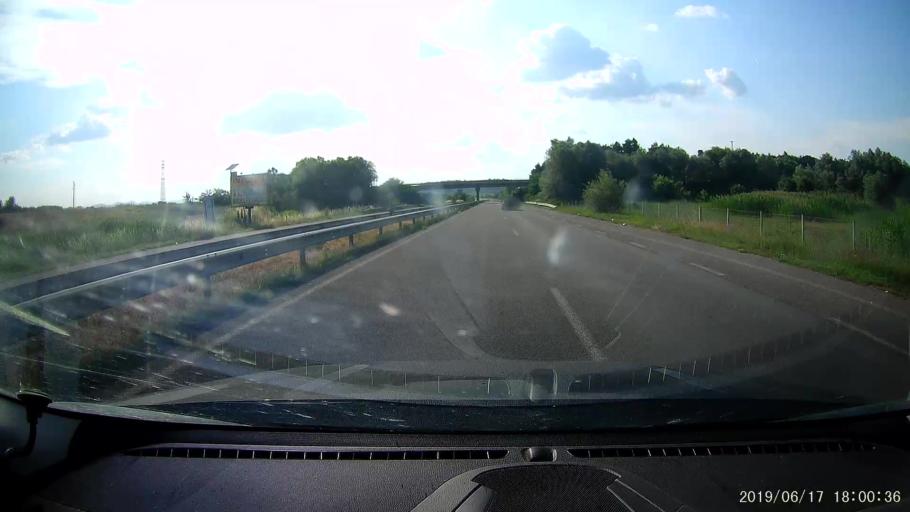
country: BG
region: Khaskovo
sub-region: Obshtina Svilengrad
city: Svilengrad
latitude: 41.7384
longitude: 26.2757
